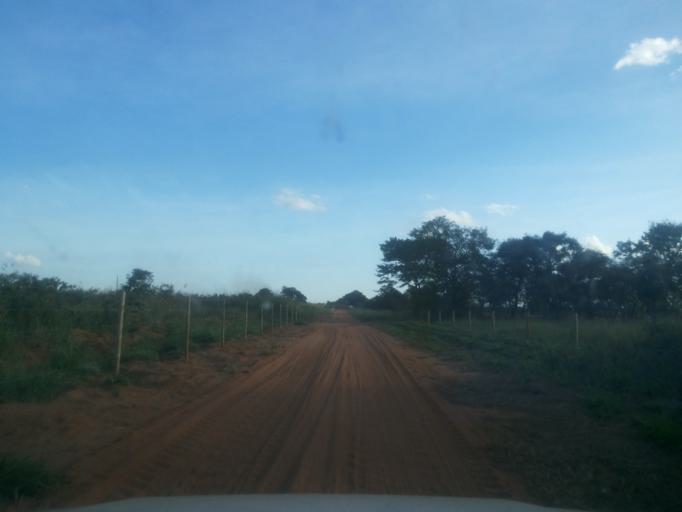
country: BR
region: Minas Gerais
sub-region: Santa Vitoria
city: Santa Vitoria
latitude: -18.9909
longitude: -50.3730
